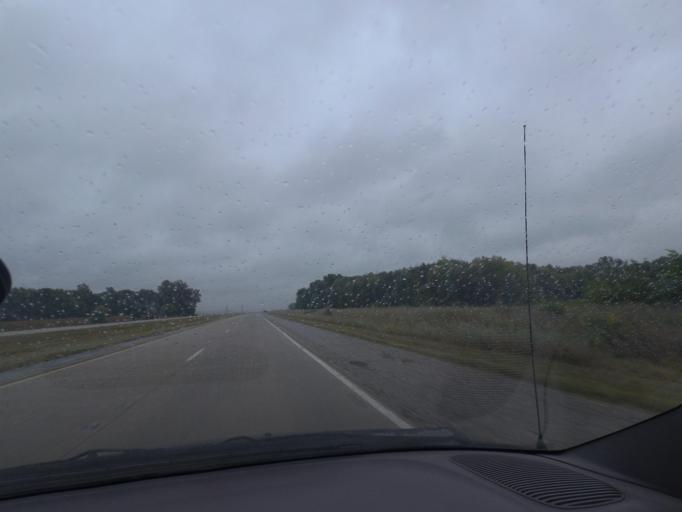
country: US
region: Illinois
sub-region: Adams County
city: Payson
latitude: 39.7377
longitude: -91.2515
